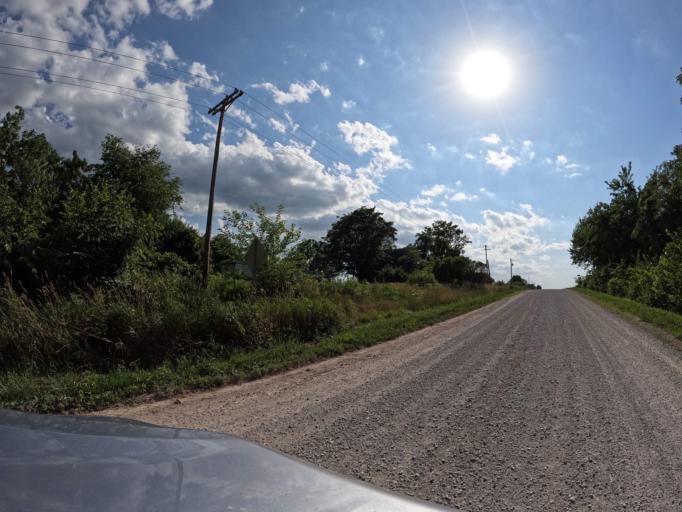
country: US
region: Iowa
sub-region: Appanoose County
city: Centerville
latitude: 40.7179
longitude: -93.0007
